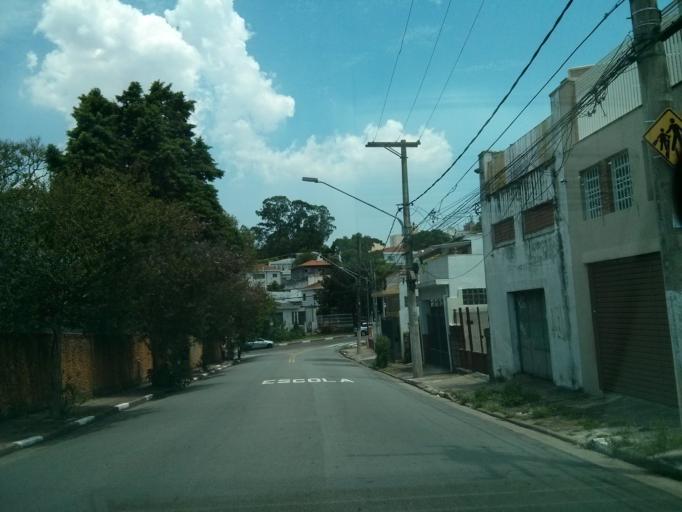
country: BR
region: Sao Paulo
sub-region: Sao Caetano Do Sul
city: Sao Caetano do Sul
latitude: -23.6137
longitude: -46.6134
